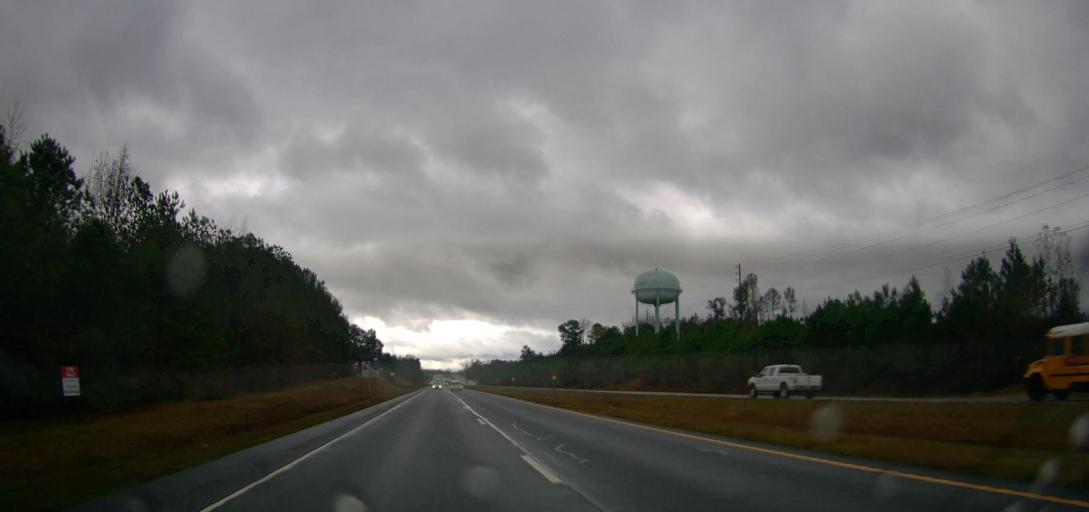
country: US
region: Georgia
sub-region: Jackson County
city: Nicholson
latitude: 34.1417
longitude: -83.4343
